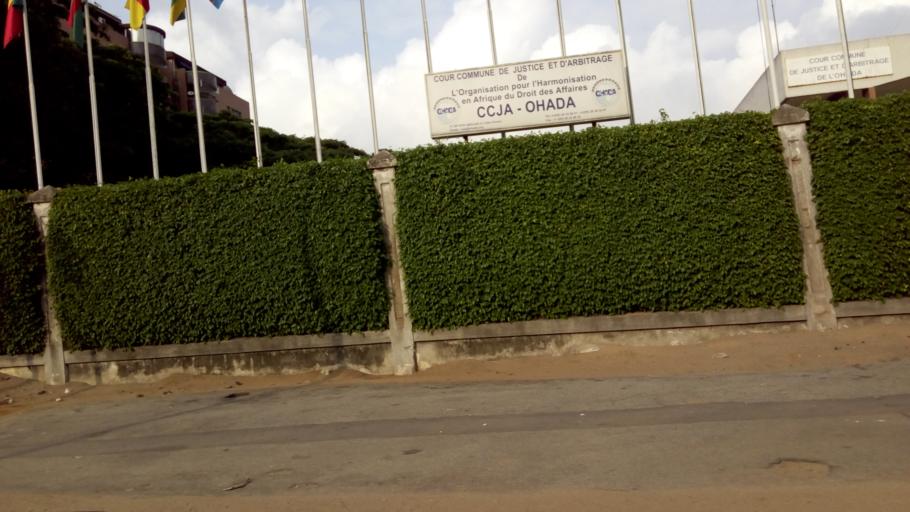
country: CI
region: Lagunes
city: Abidjan
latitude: 5.3293
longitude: -4.0239
